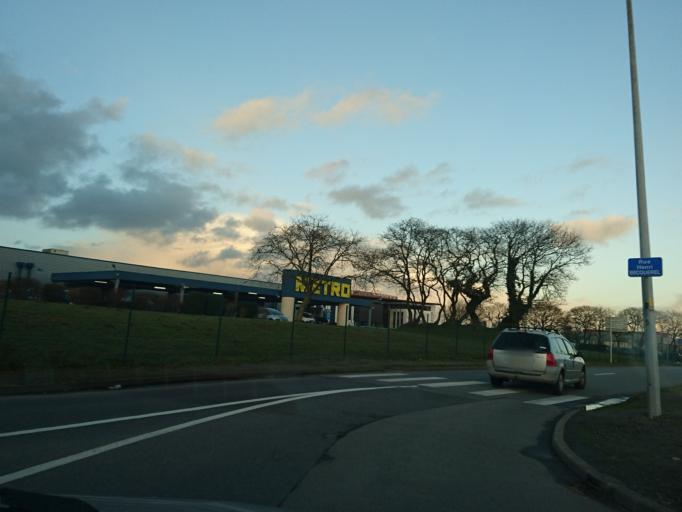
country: FR
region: Brittany
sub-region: Departement du Finistere
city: Gouesnou
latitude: 48.4314
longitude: -4.4524
